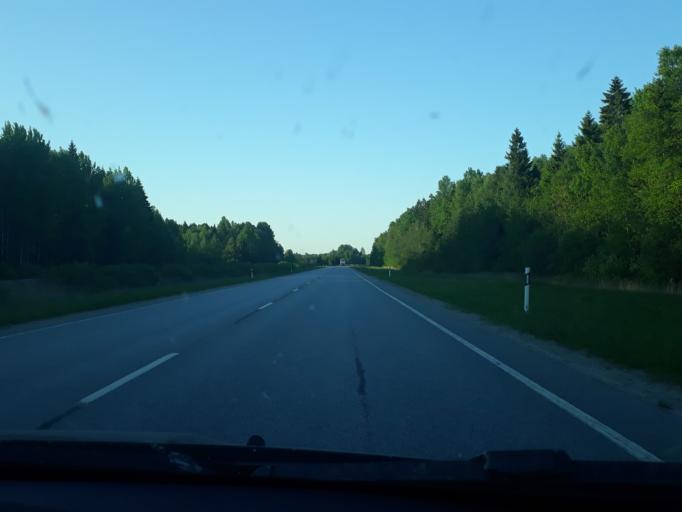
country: EE
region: Paernumaa
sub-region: Sindi linn
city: Sindi
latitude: 58.4562
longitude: 24.6963
